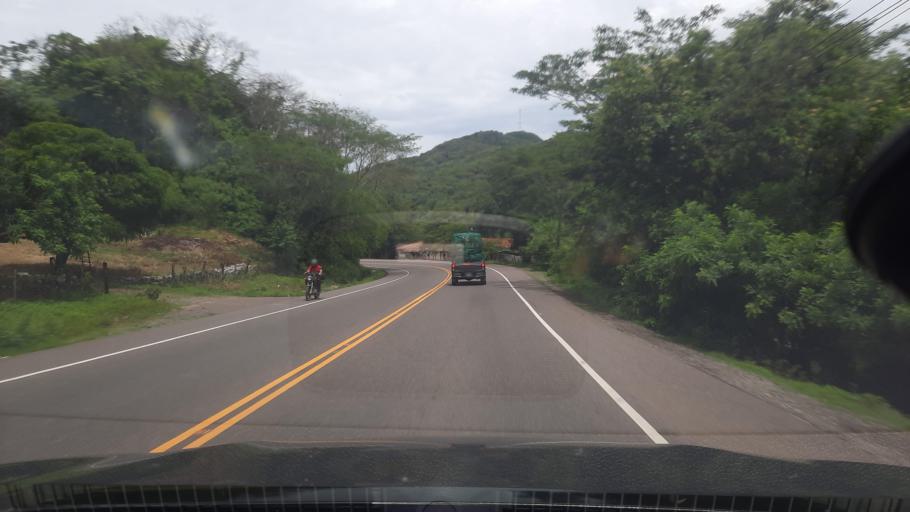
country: HN
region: Valle
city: Goascoran
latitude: 13.5643
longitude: -87.6711
